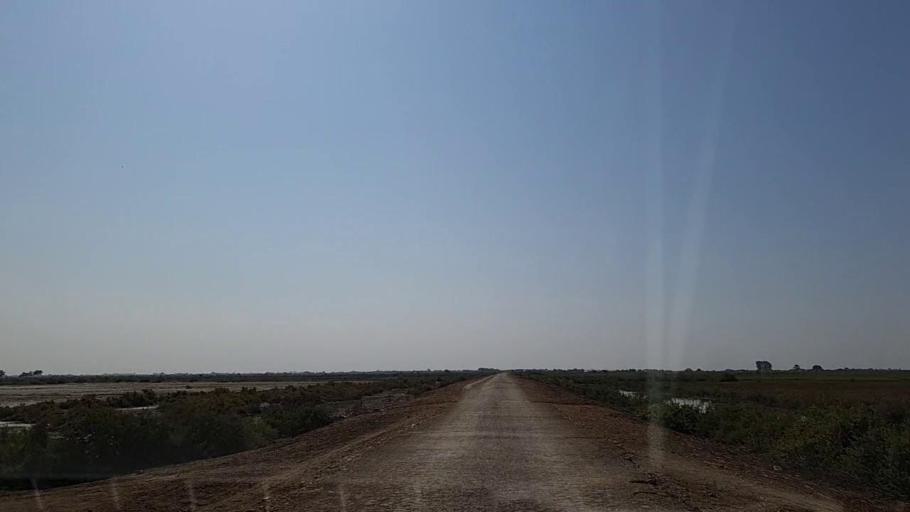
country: PK
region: Sindh
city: Chuhar Jamali
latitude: 24.4811
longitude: 68.0918
